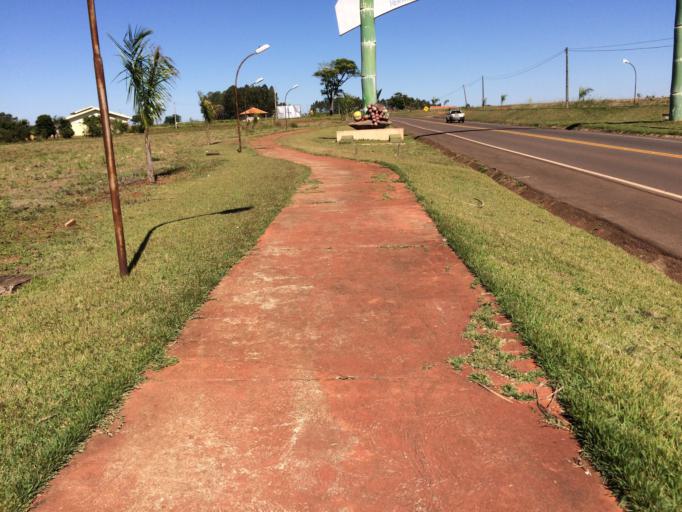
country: BR
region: Parana
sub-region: Cianorte
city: Cianorte
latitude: -23.5391
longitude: -52.5994
